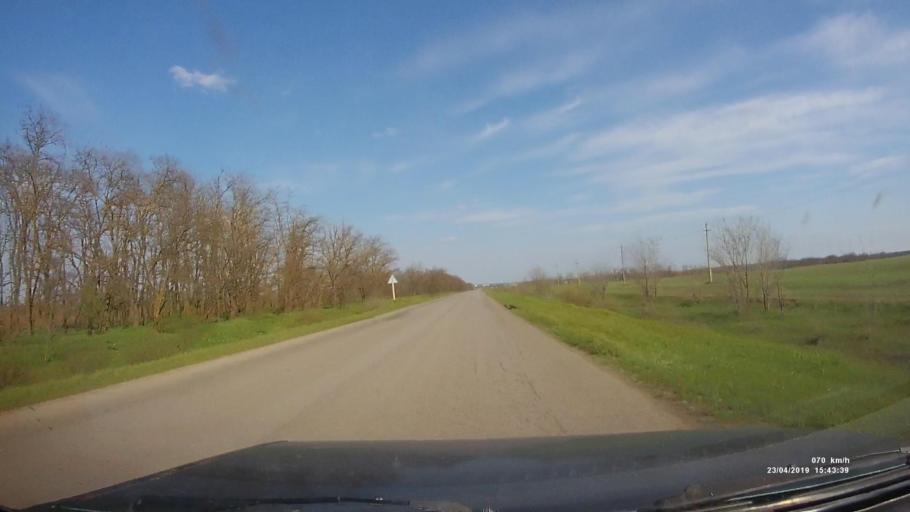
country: RU
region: Rostov
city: Remontnoye
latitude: 46.5442
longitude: 43.0857
